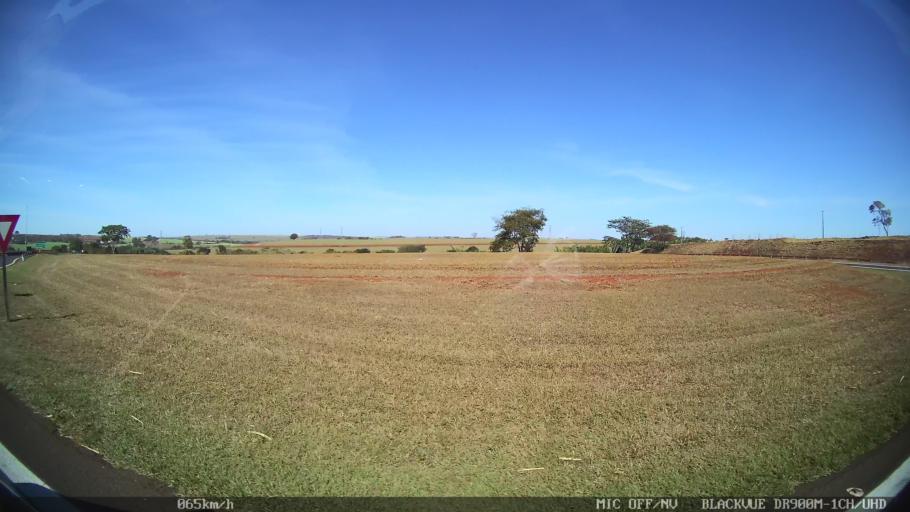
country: BR
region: Sao Paulo
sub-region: Sao Joaquim Da Barra
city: Sao Joaquim da Barra
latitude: -20.5241
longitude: -47.8422
